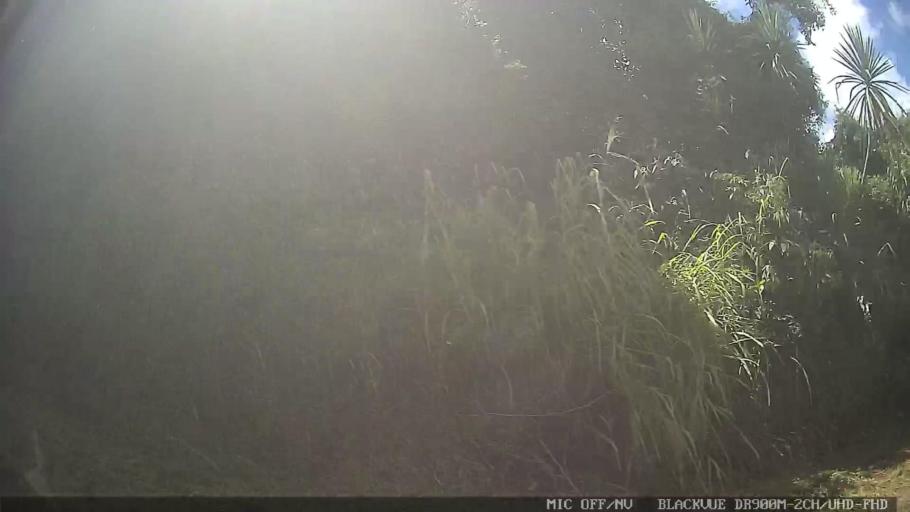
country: BR
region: Sao Paulo
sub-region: Amparo
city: Amparo
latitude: -22.8315
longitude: -46.7028
